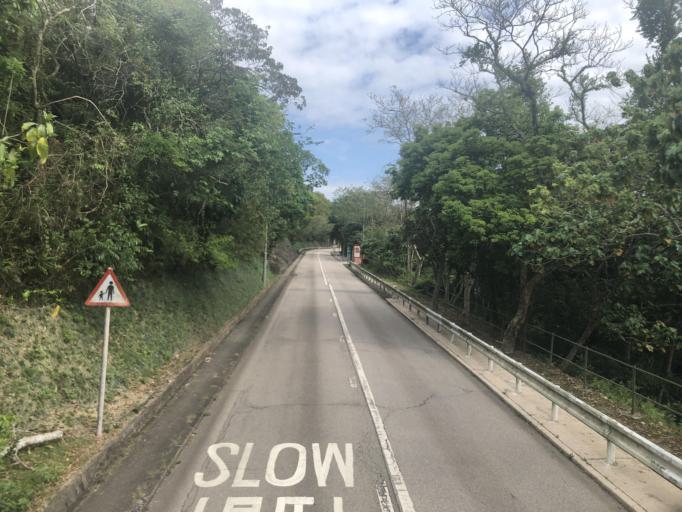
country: HK
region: Sai Kung
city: Sai Kung
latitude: 22.3893
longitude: 114.3016
